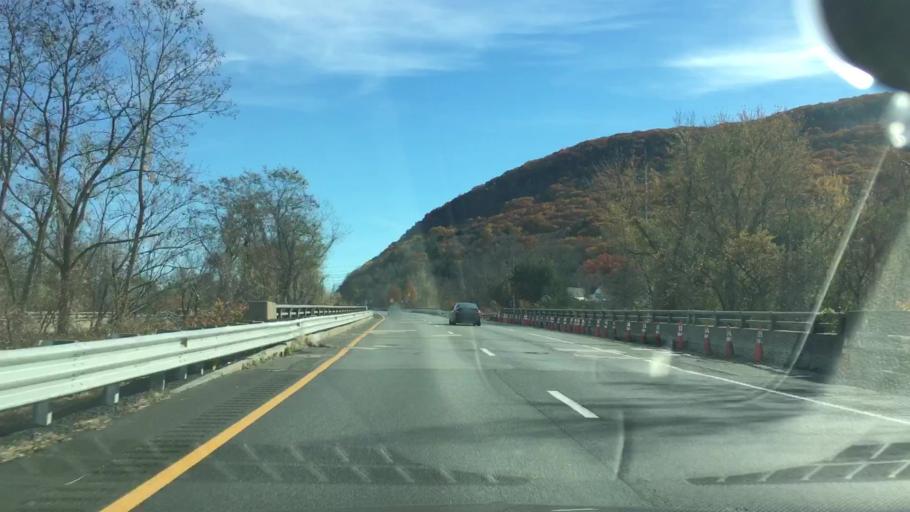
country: US
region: Massachusetts
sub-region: Hampshire County
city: Northampton
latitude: 42.2882
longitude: -72.6237
